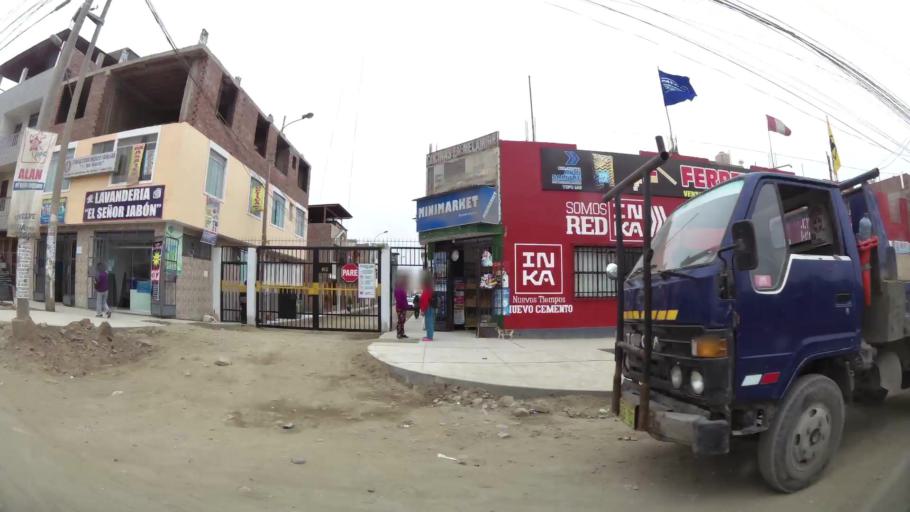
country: PE
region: Lima
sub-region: Lima
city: Surco
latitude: -12.1979
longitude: -76.9672
